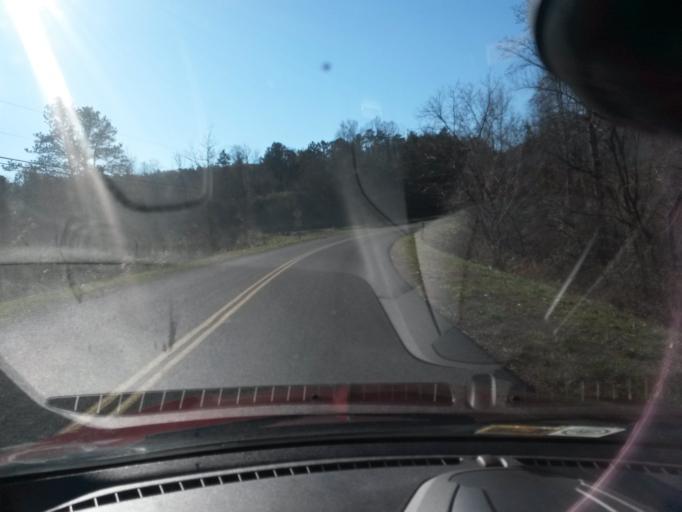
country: US
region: Virginia
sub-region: Alleghany County
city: Clifton Forge
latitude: 37.7743
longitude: -79.7805
